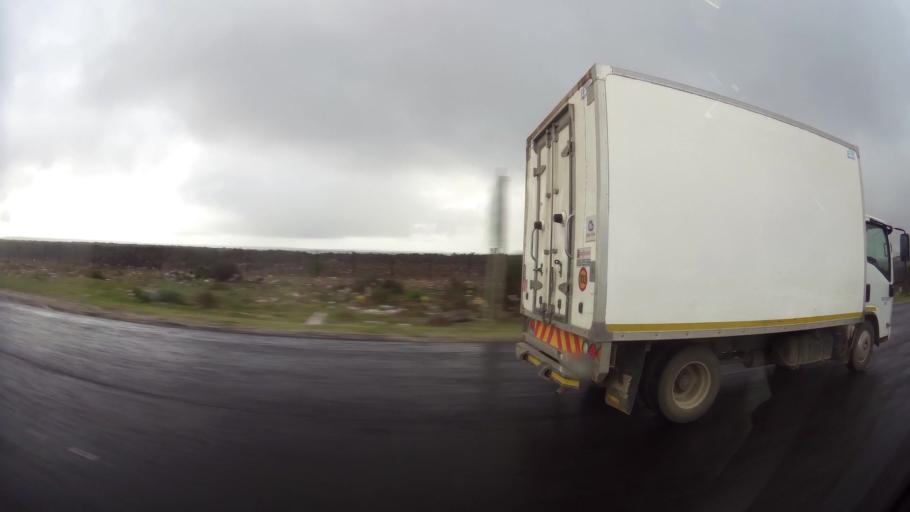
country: ZA
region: Eastern Cape
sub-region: Nelson Mandela Bay Metropolitan Municipality
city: Port Elizabeth
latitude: -33.8337
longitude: 25.5173
